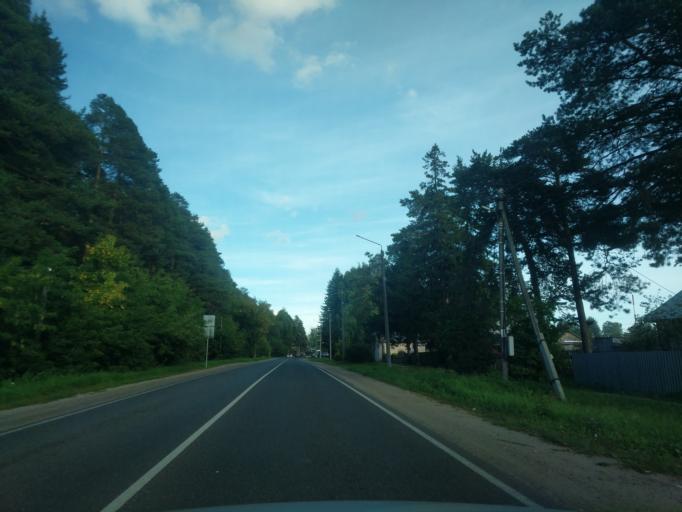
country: RU
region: Kirov
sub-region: Kirovo-Chepetskiy Rayon
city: Kirov
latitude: 58.6108
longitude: 49.7950
